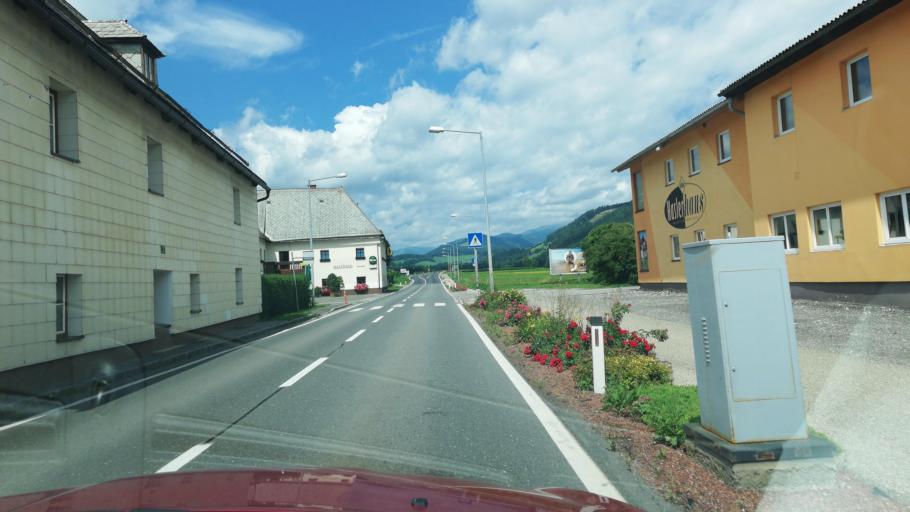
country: AT
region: Styria
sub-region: Politischer Bezirk Murtal
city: Oberzeiring
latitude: 47.2446
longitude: 14.5314
